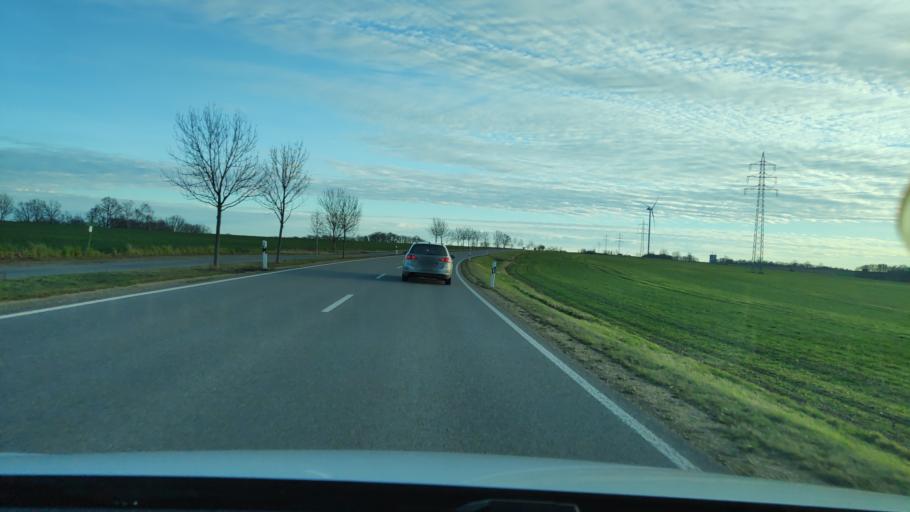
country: DE
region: Saxony
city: Mulsen
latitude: 50.7524
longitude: 12.5505
